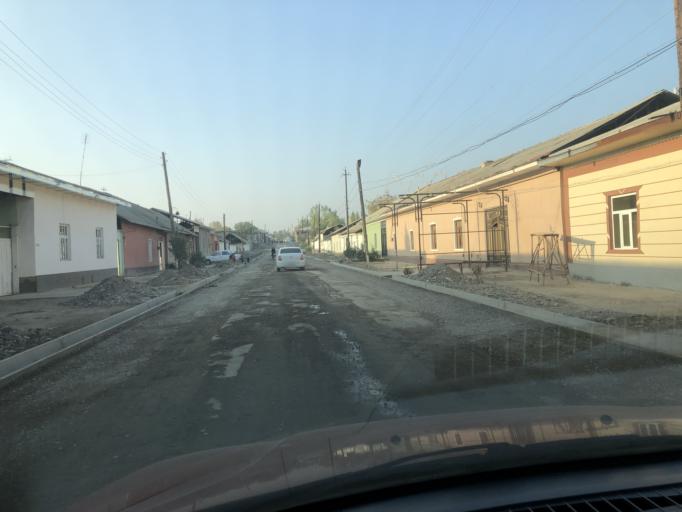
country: UZ
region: Namangan
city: Uychi
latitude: 41.0795
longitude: 72.0010
